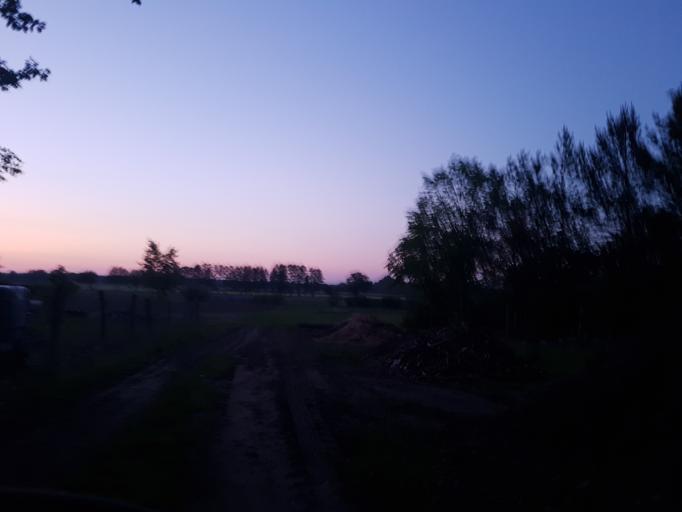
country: DE
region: Brandenburg
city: Bad Liebenwerda
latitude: 51.5587
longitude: 13.4038
